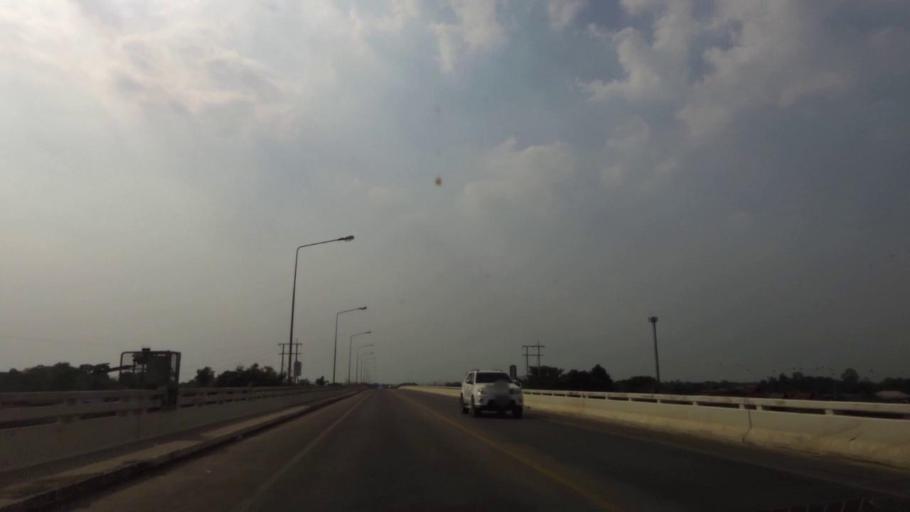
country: TH
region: Phra Nakhon Si Ayutthaya
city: Phra Nakhon Si Ayutthaya
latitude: 14.3036
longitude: 100.5670
